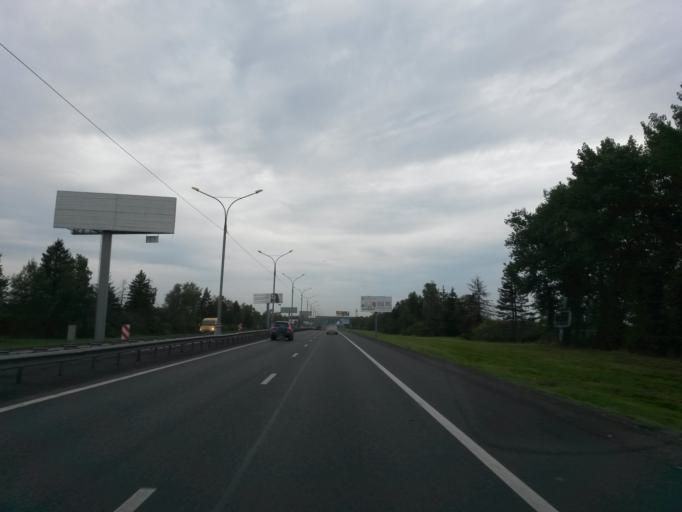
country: RU
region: Moskovskaya
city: Petrovskaya
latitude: 55.5239
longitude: 37.8202
